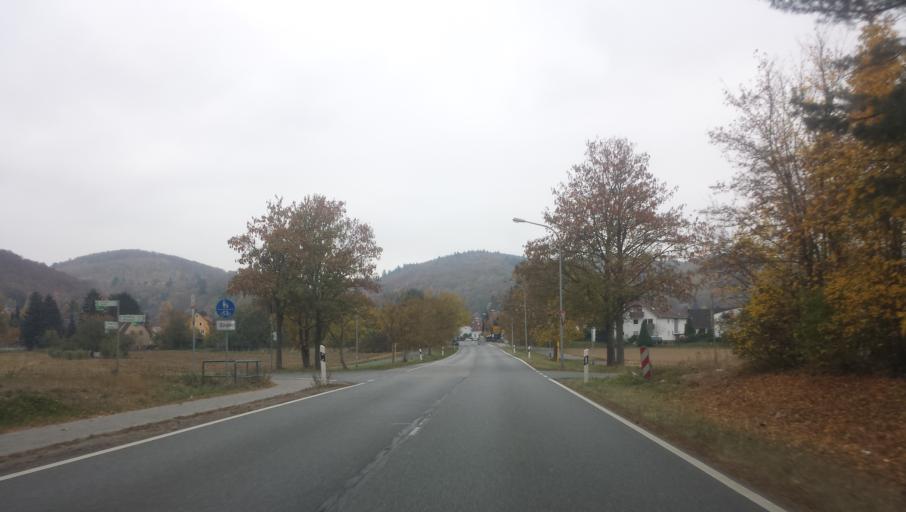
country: DE
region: Hesse
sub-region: Regierungsbezirk Darmstadt
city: Bickenbach
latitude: 49.7596
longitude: 8.6322
